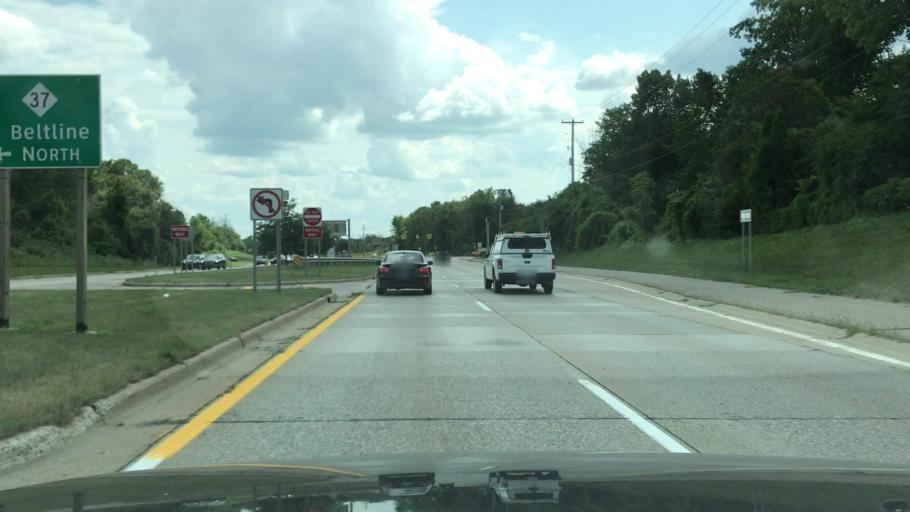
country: US
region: Michigan
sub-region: Kent County
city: East Grand Rapids
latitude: 42.9585
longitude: -85.5902
